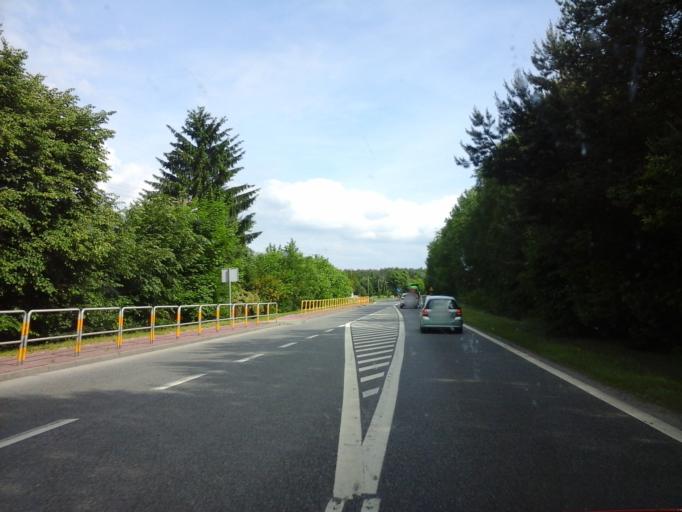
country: PL
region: Lodz Voivodeship
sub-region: Powiat opoczynski
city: Paradyz
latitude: 51.2984
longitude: 20.1199
